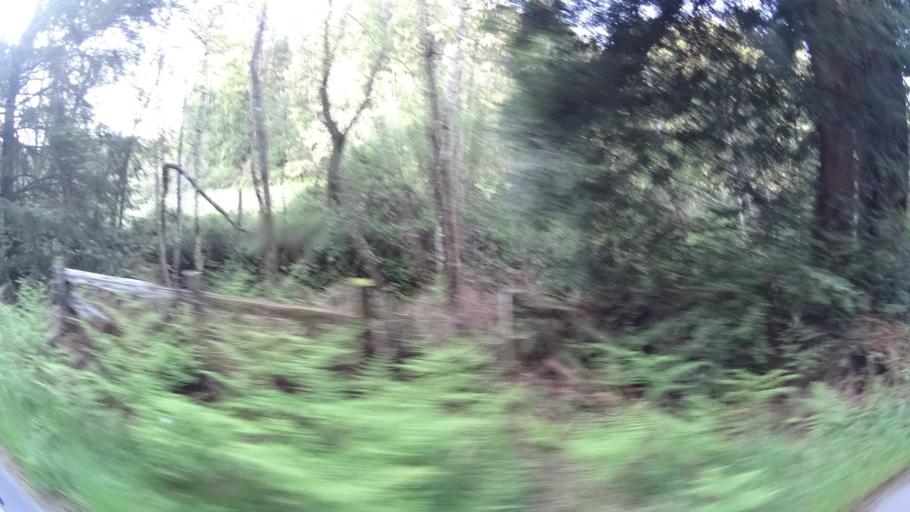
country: US
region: California
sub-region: Humboldt County
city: Myrtletown
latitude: 40.7768
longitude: -124.1145
